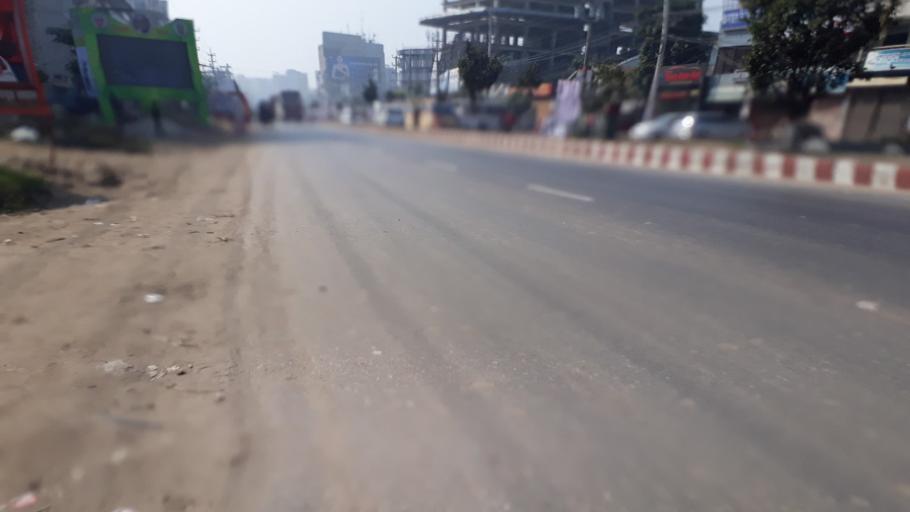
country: BD
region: Dhaka
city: Tungi
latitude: 23.8582
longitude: 90.2622
